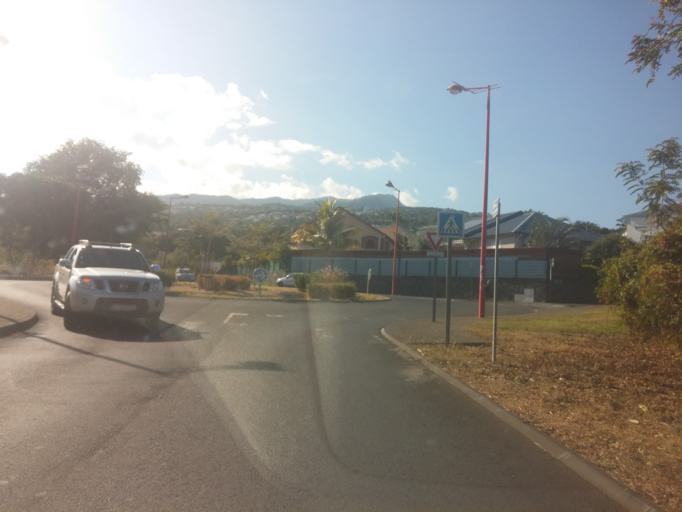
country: RE
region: Reunion
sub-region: Reunion
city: La Possession
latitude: -20.9629
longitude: 55.3281
